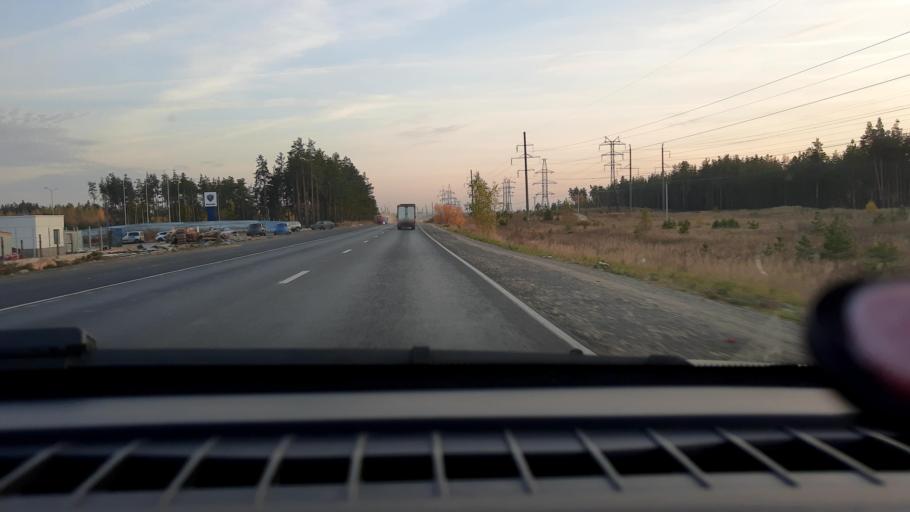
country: RU
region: Nizjnij Novgorod
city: Babino
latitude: 56.3067
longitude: 43.5594
